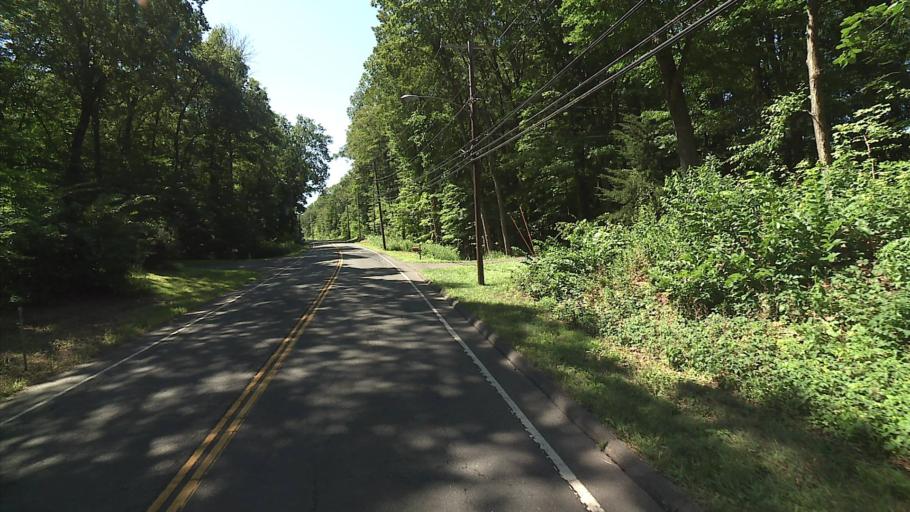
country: US
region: Connecticut
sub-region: Hartford County
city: Farmington
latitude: 41.7392
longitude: -72.8203
